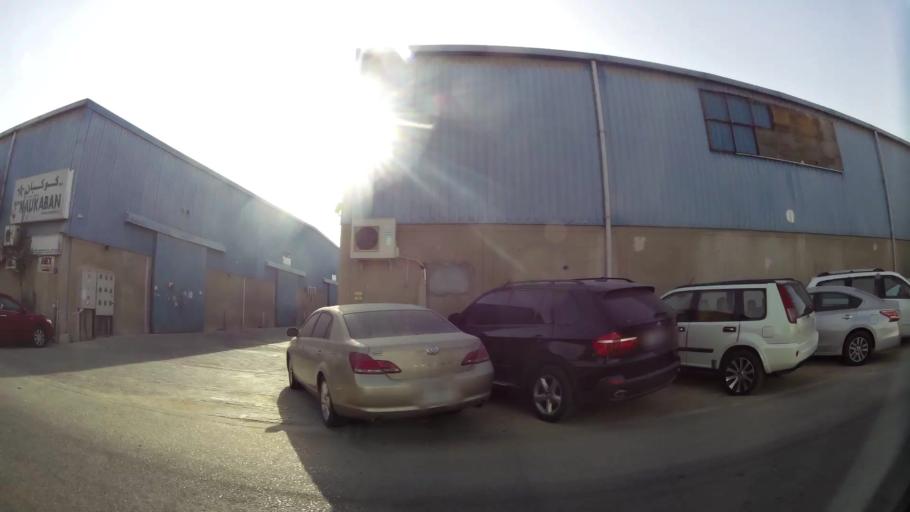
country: AE
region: Ash Shariqah
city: Sharjah
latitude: 25.2324
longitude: 55.3734
